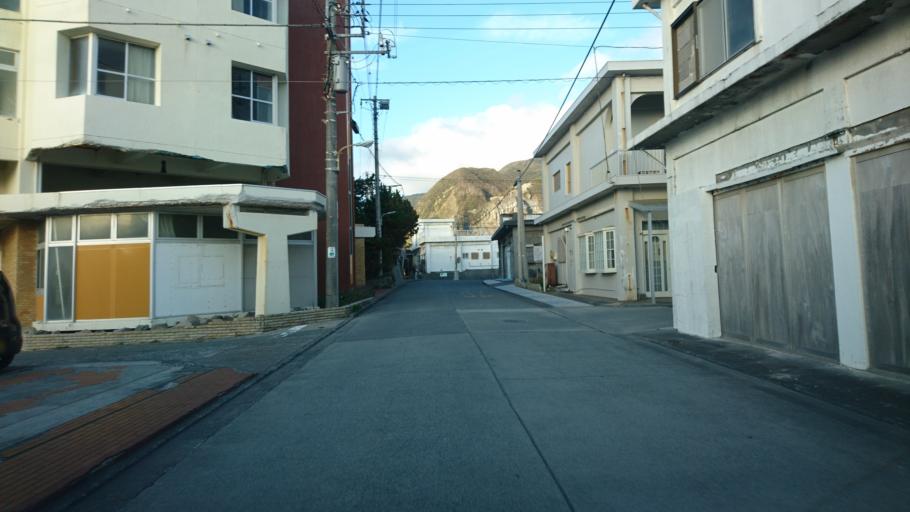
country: JP
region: Shizuoka
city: Shimoda
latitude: 34.3768
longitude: 139.2537
